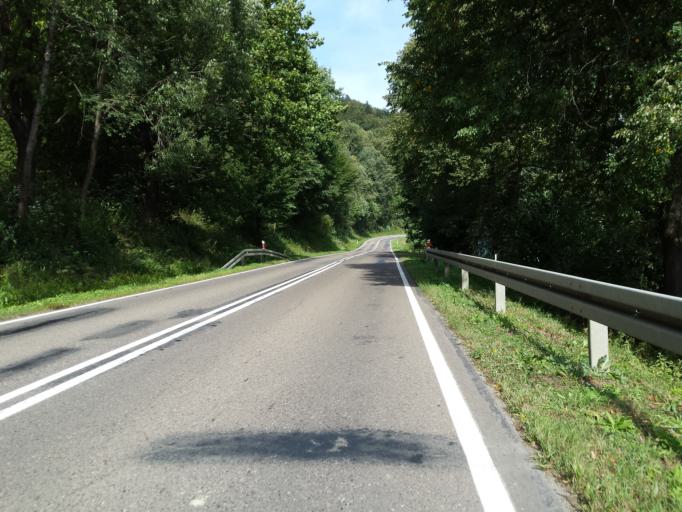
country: PL
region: Subcarpathian Voivodeship
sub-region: Powiat leski
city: Baligrod
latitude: 49.3659
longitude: 22.2732
